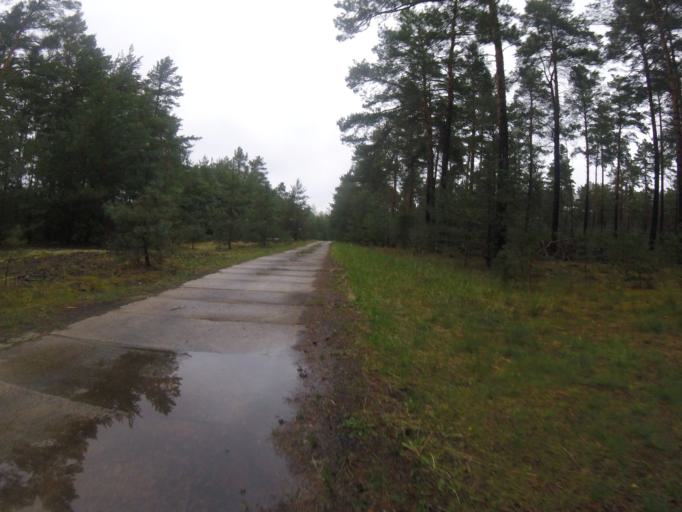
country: DE
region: Brandenburg
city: Schwerin
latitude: 52.1479
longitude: 13.6514
